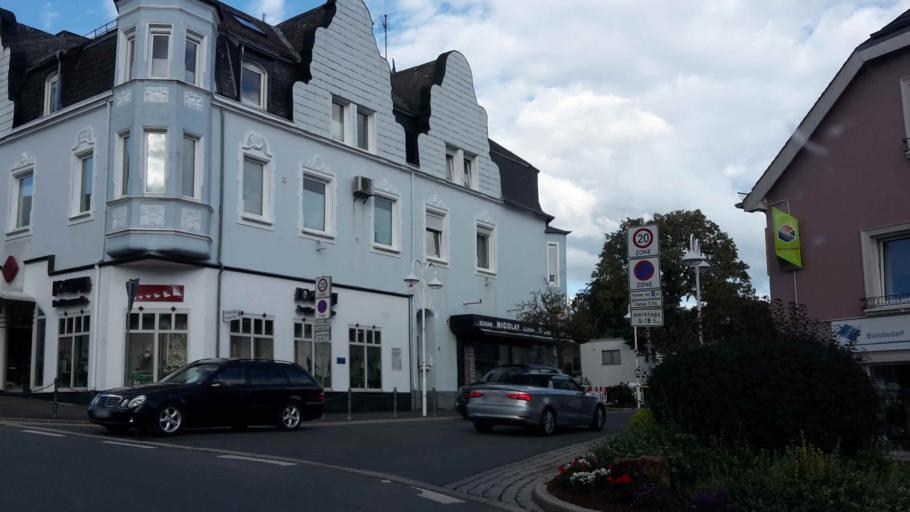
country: DE
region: North Rhine-Westphalia
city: Halver
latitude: 51.1867
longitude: 7.4990
